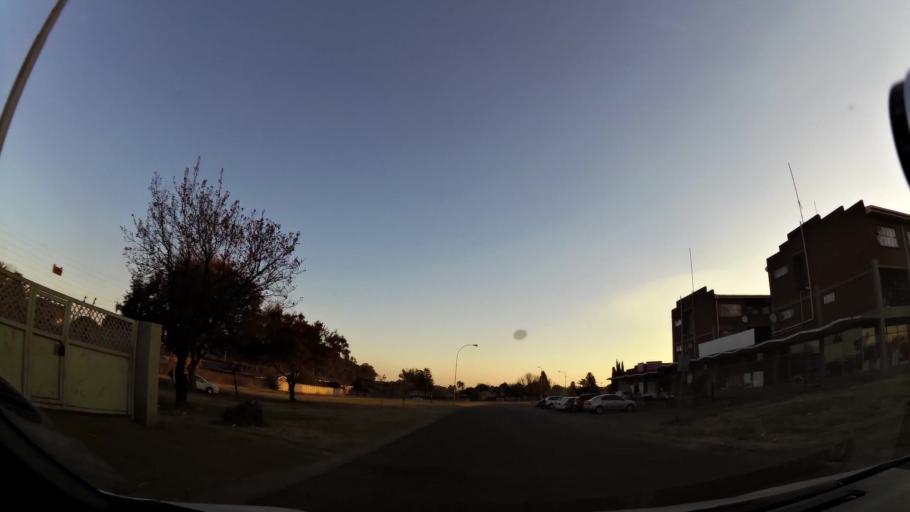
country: ZA
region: Gauteng
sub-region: Ekurhuleni Metropolitan Municipality
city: Germiston
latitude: -26.2710
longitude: 28.1608
